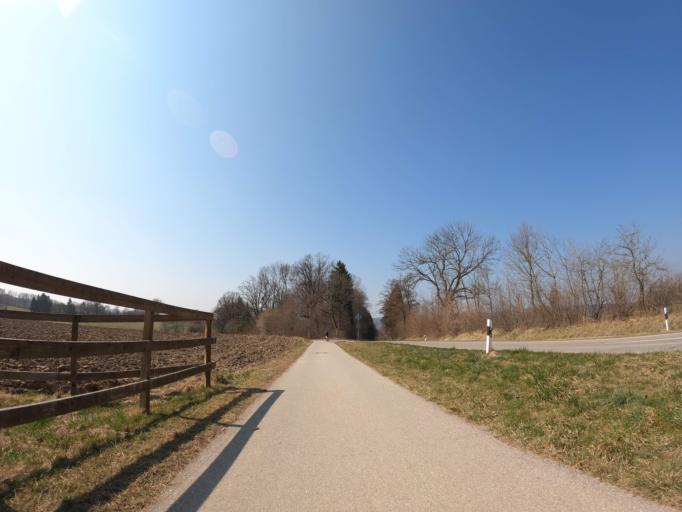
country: DE
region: Bavaria
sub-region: Upper Bavaria
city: Starnberg
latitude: 48.0000
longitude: 11.3745
